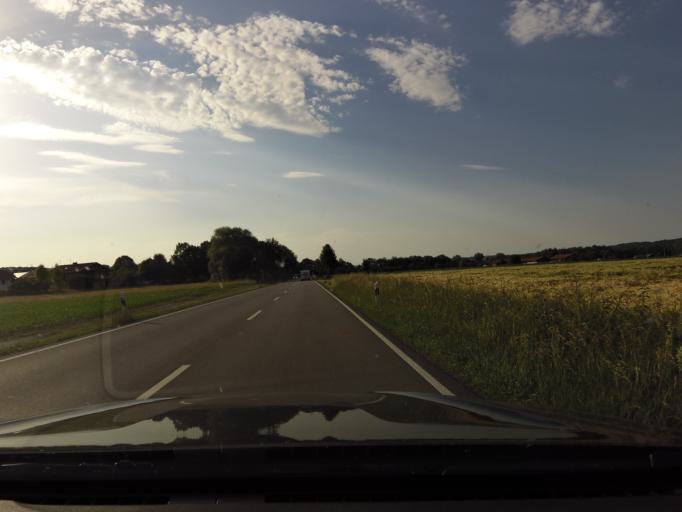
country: DE
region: Bavaria
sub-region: Upper Bavaria
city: Tittmoning
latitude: 48.0391
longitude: 12.7883
